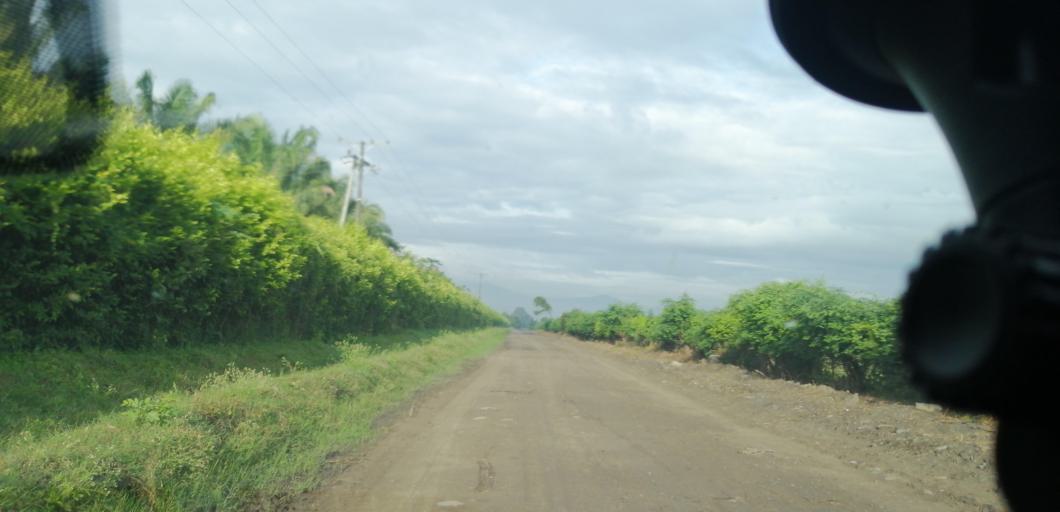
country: CO
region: Valle del Cauca
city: Palmira
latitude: 3.5531
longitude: -76.3642
